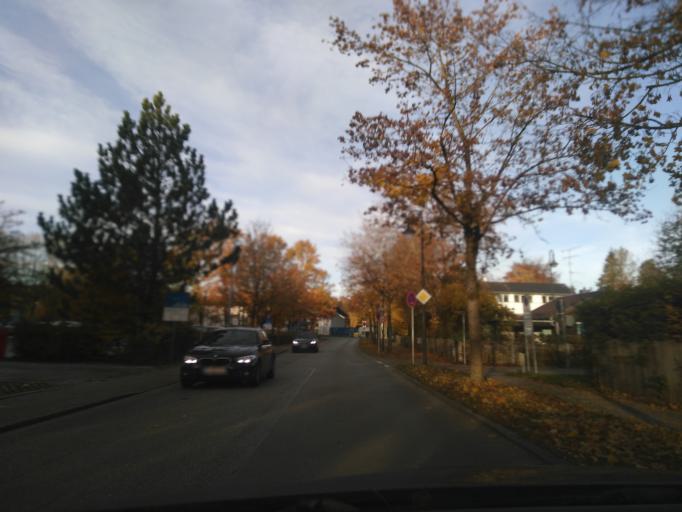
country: DE
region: Bavaria
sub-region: Upper Bavaria
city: Grunwald
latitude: 48.0456
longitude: 11.5093
